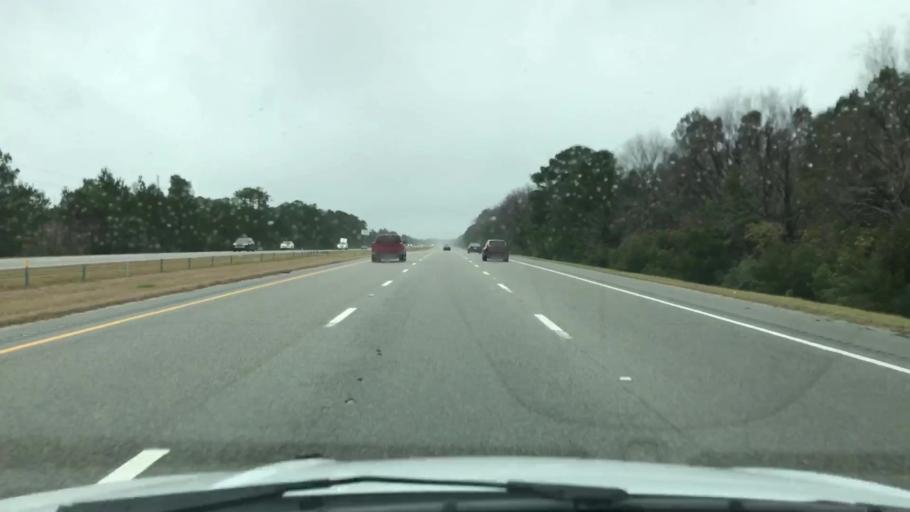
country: US
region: South Carolina
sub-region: Horry County
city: Myrtle Beach
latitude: 33.7499
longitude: -78.9012
